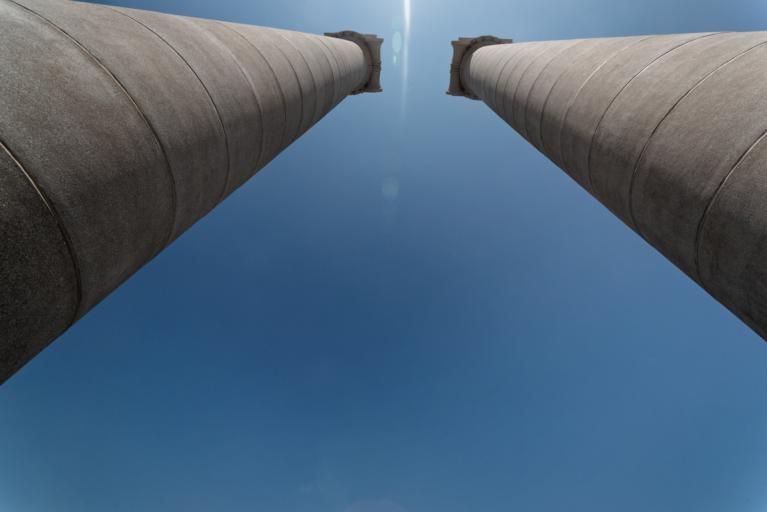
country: ES
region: Catalonia
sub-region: Provincia de Barcelona
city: Sants-Montjuic
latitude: 41.3707
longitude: 2.1520
